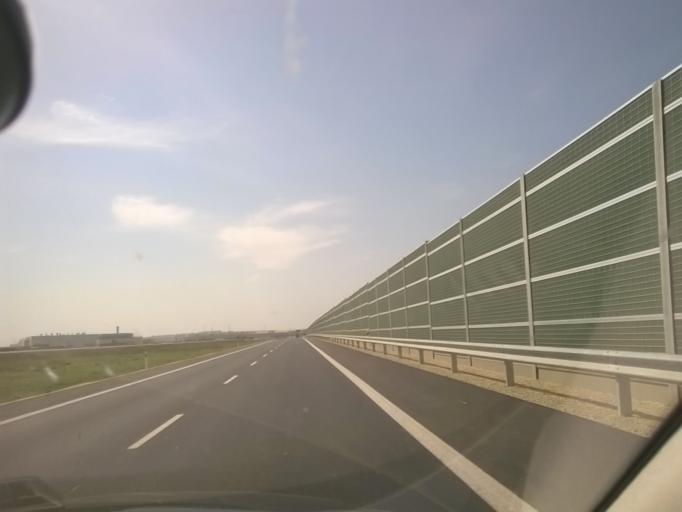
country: SK
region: Nitriansky
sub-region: Okres Nitra
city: Nitra
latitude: 48.3608
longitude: 18.0379
